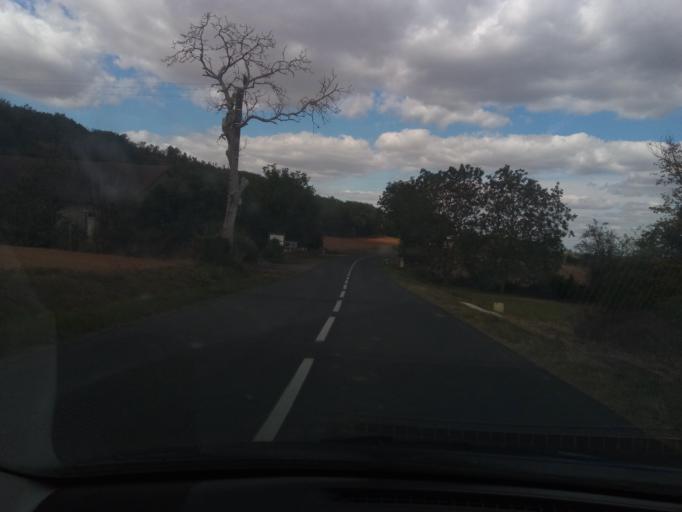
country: FR
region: Poitou-Charentes
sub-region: Departement de la Vienne
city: Saint-Savin
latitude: 46.5464
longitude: 0.8597
